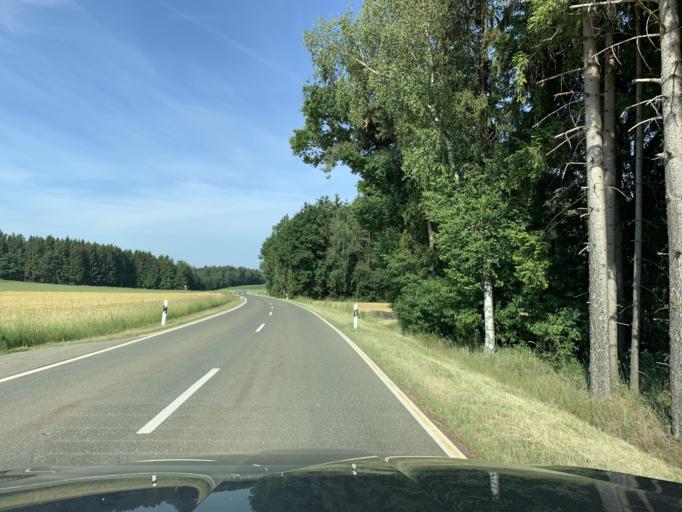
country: DE
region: Bavaria
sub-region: Upper Palatinate
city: Bach
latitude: 49.4190
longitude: 12.3920
